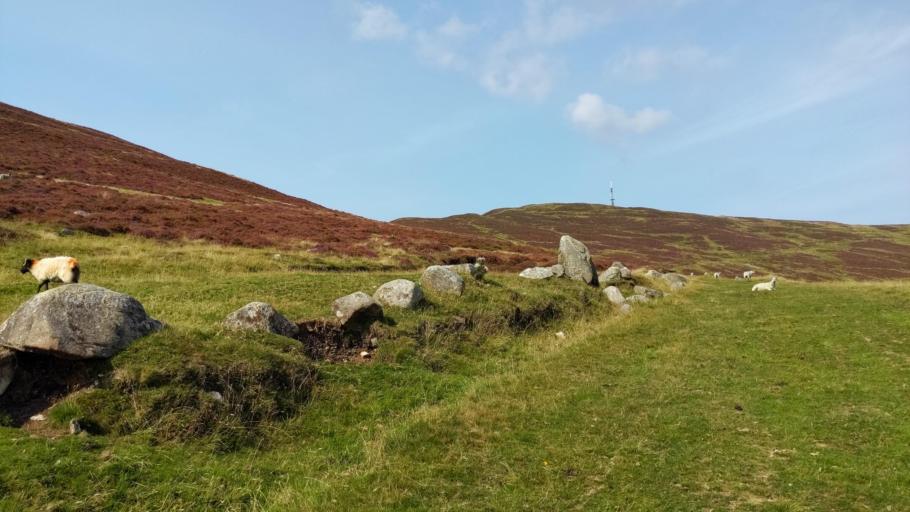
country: GB
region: Northern Ireland
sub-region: Down District
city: Warrenpoint
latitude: 54.0684
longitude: -6.3257
